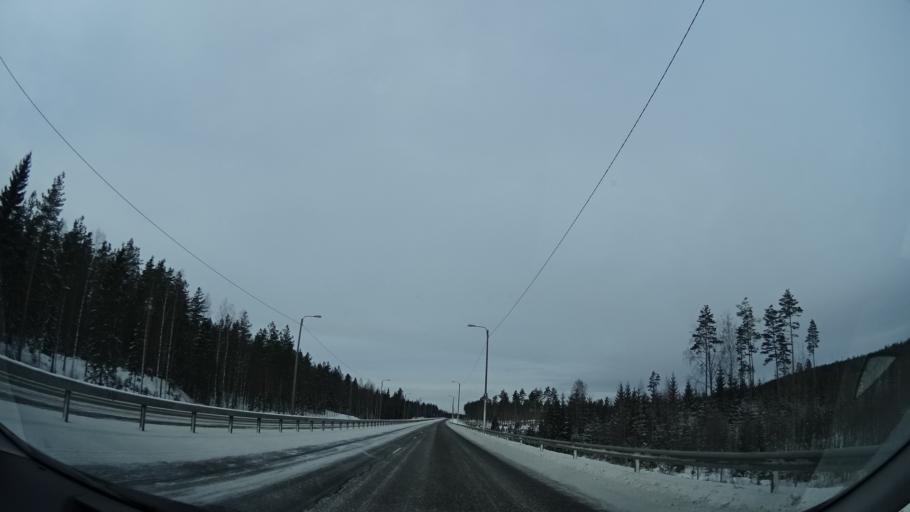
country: FI
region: Uusimaa
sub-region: Helsinki
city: Kaerkoelae
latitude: 60.6336
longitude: 23.9119
